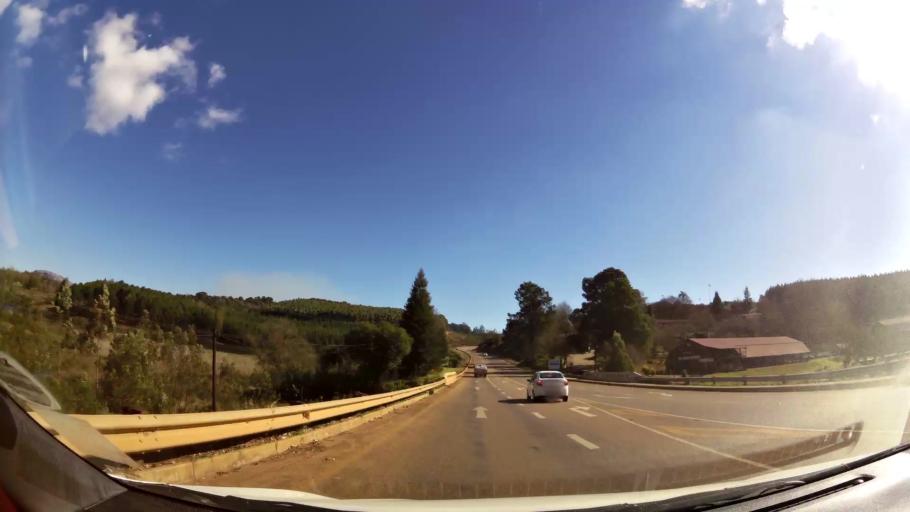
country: ZA
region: Limpopo
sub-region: Capricorn District Municipality
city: Mankoeng
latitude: -23.9102
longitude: 29.9763
